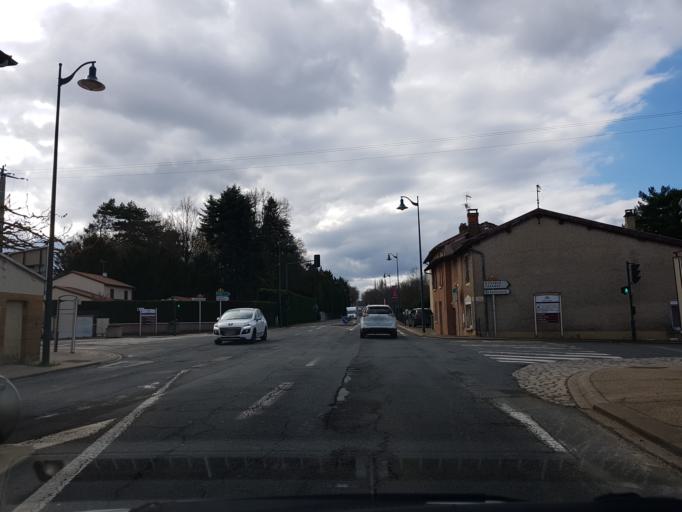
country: FR
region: Rhone-Alpes
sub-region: Departement du Rhone
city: Les Cheres
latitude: 45.8872
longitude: 4.7436
